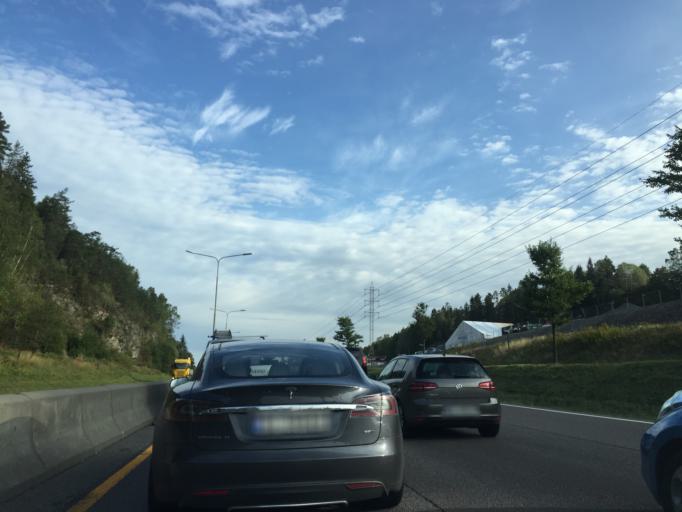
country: NO
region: Akershus
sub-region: Oppegard
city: Kolbotn
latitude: 59.8653
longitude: 10.8305
